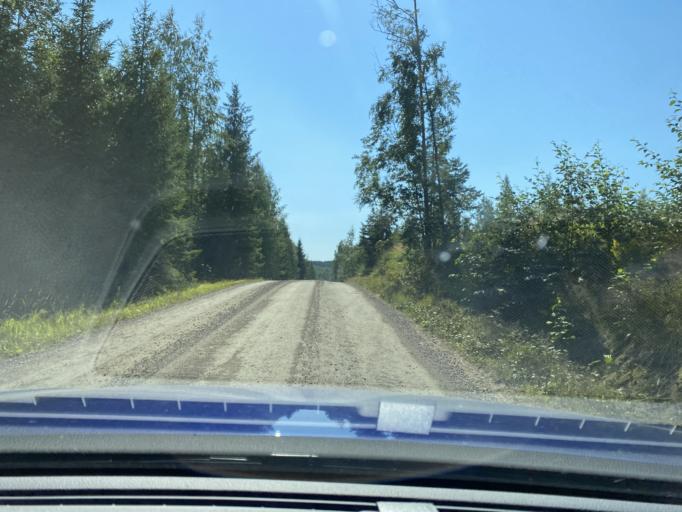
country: FI
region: Central Finland
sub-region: Jyvaeskylae
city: Korpilahti
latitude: 61.8689
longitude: 25.4218
